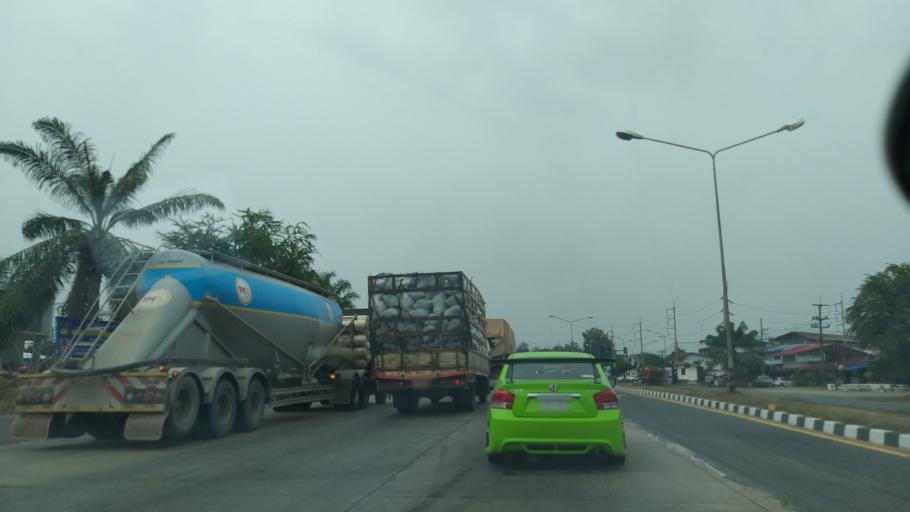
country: TH
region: Chon Buri
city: Ko Chan
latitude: 13.3236
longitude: 101.2699
